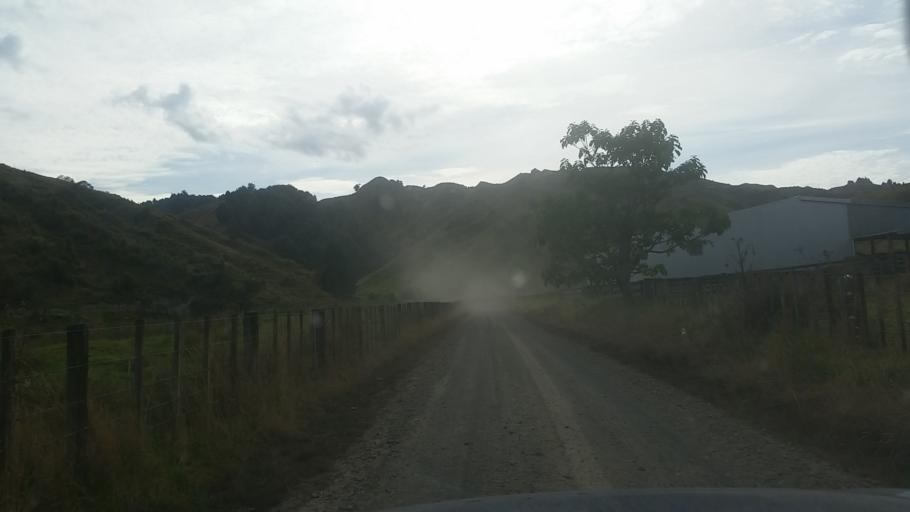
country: NZ
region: Taranaki
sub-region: New Plymouth District
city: Waitara
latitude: -39.1283
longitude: 174.6937
